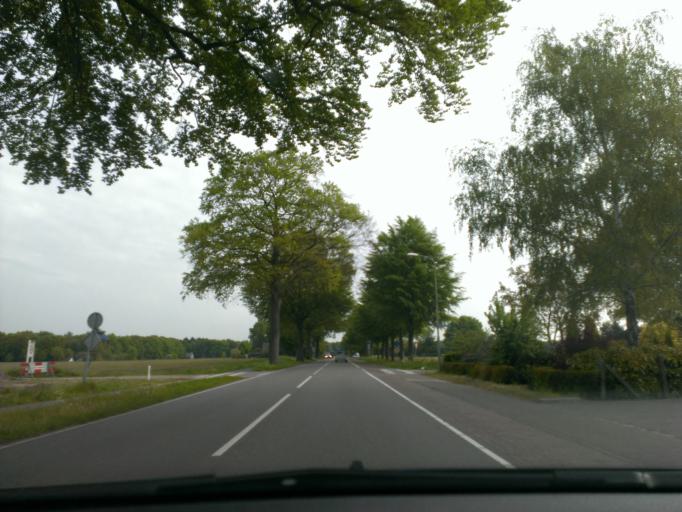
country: NL
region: Gelderland
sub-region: Gemeente Heerde
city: Heerde
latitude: 52.4024
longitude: 6.0511
